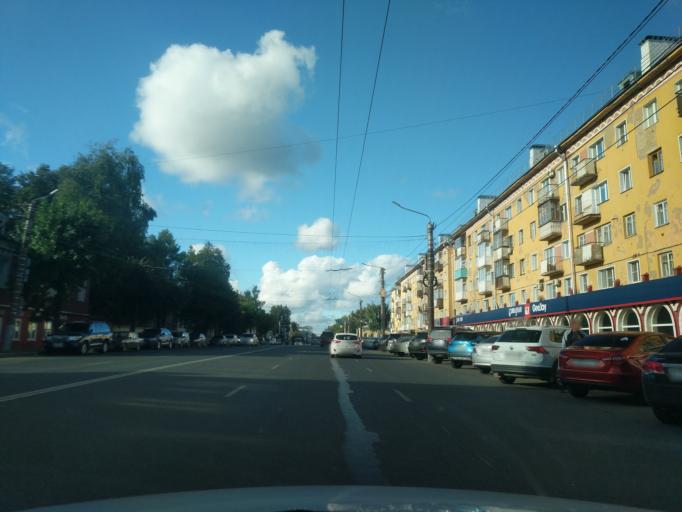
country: RU
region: Kirov
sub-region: Kirovo-Chepetskiy Rayon
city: Kirov
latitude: 58.5949
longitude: 49.6818
